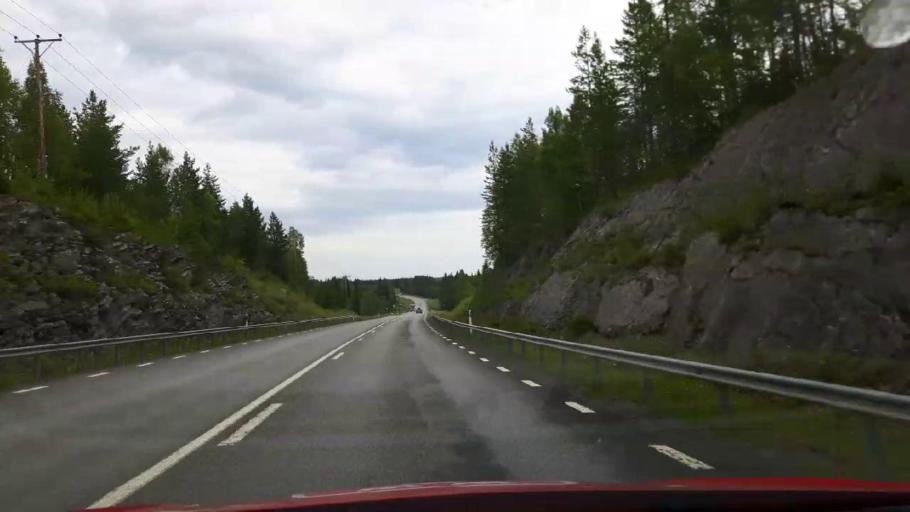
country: SE
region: Jaemtland
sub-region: Stroemsunds Kommun
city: Stroemsund
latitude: 63.6368
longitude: 15.3611
